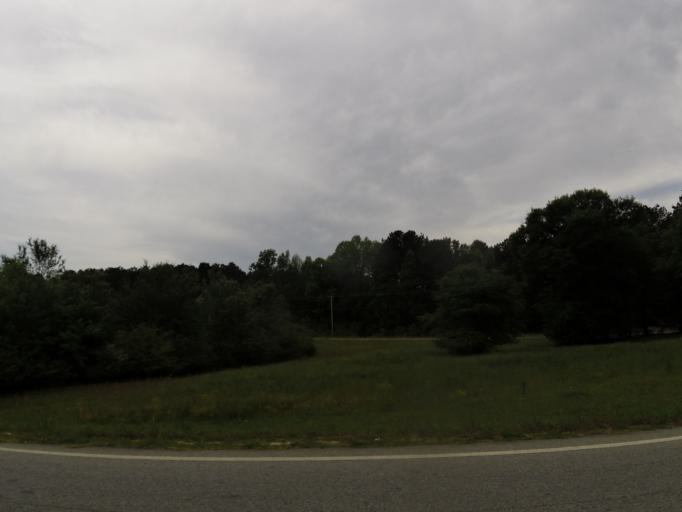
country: US
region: Georgia
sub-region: Candler County
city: Metter
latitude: 32.4316
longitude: -82.2138
